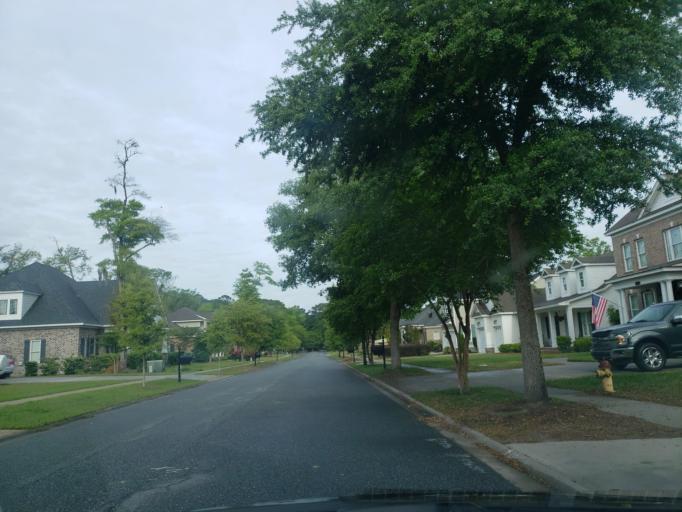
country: US
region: Georgia
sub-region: Chatham County
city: Isle of Hope
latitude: 32.0047
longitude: -81.0683
